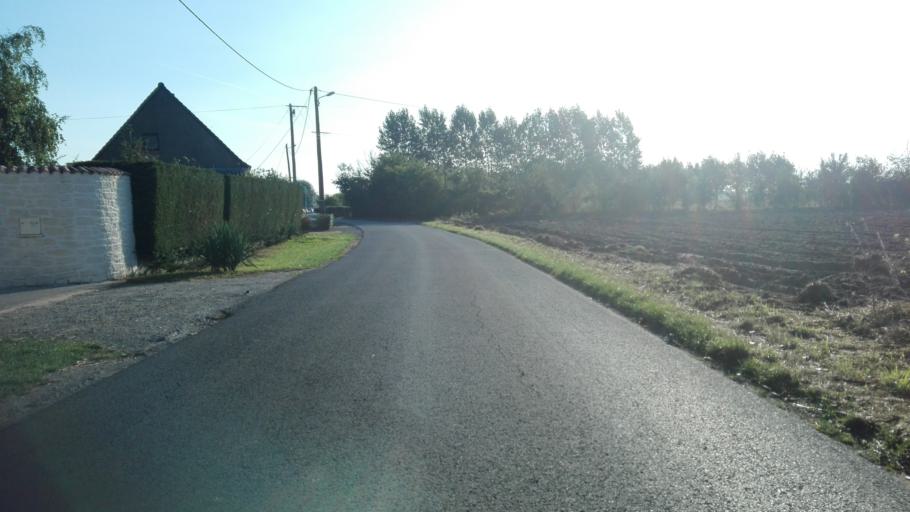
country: FR
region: Nord-Pas-de-Calais
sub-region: Departement du Nord
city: Zuydcoote
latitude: 51.0506
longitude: 2.5075
